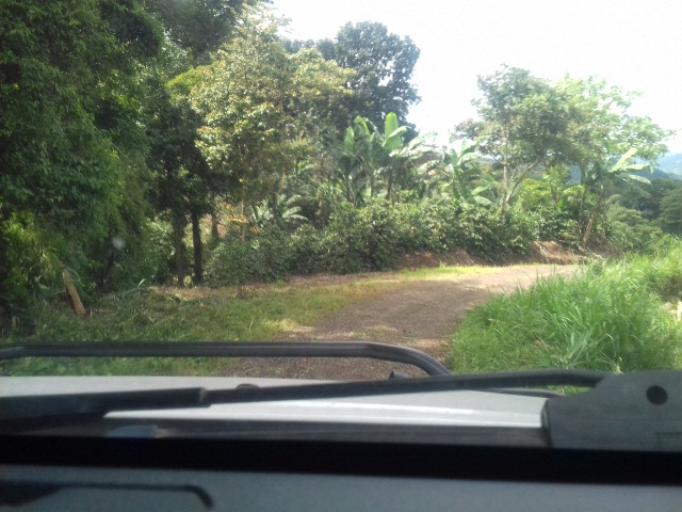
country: NI
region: Atlantico Norte (RAAN)
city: Waslala
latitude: 13.2164
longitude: -85.5755
